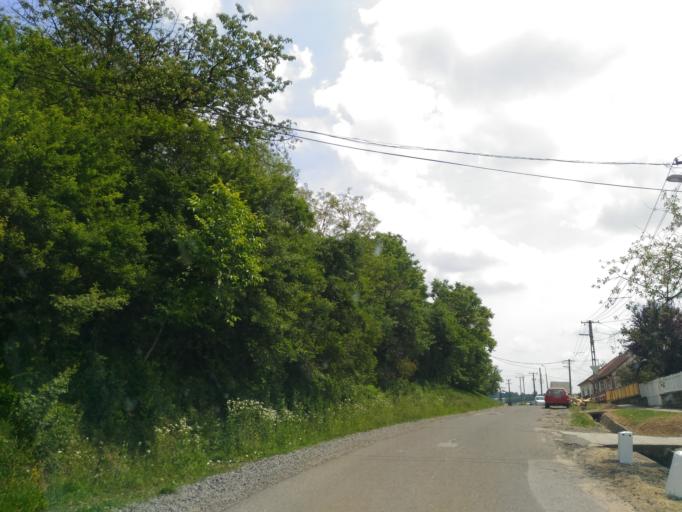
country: HU
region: Baranya
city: Komlo
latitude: 46.1949
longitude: 18.2308
